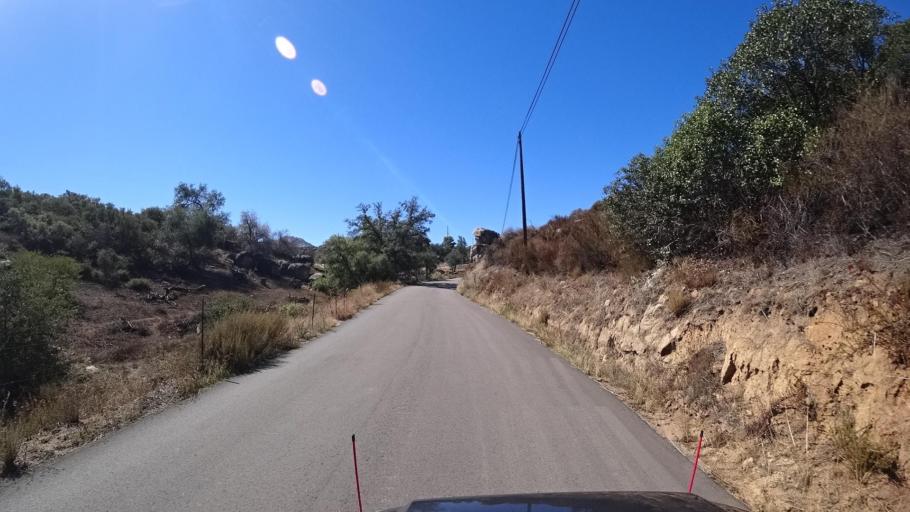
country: US
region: California
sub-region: San Diego County
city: Alpine
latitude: 32.7650
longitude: -116.6930
